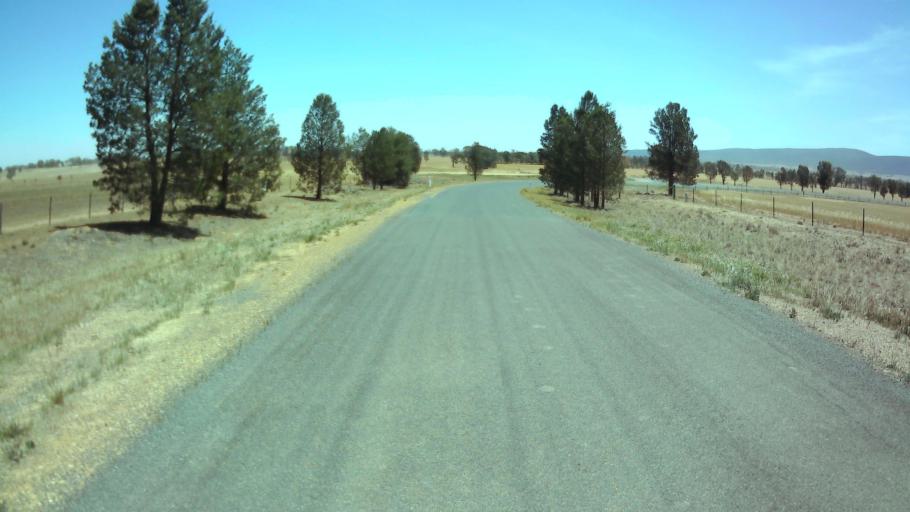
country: AU
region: New South Wales
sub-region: Weddin
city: Grenfell
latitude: -34.0496
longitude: 148.1748
